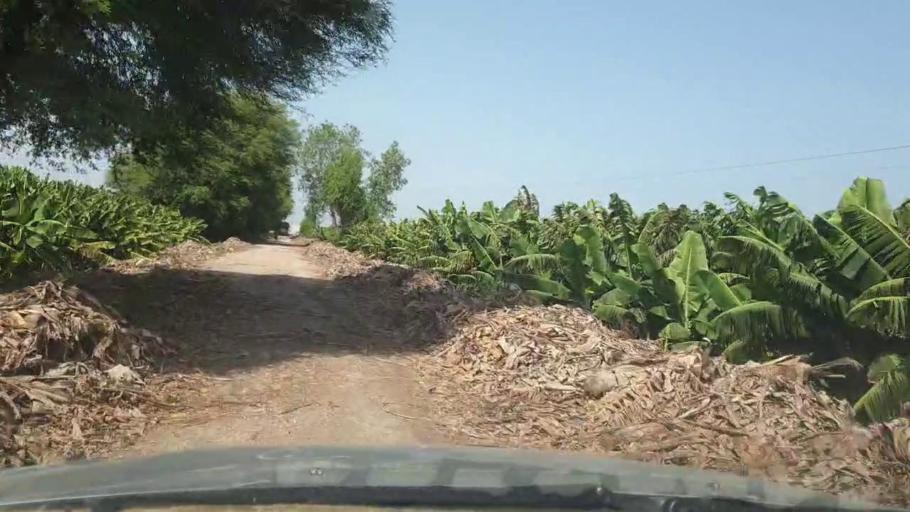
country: PK
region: Sindh
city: Tando Ghulam Ali
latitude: 25.1481
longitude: 68.8860
